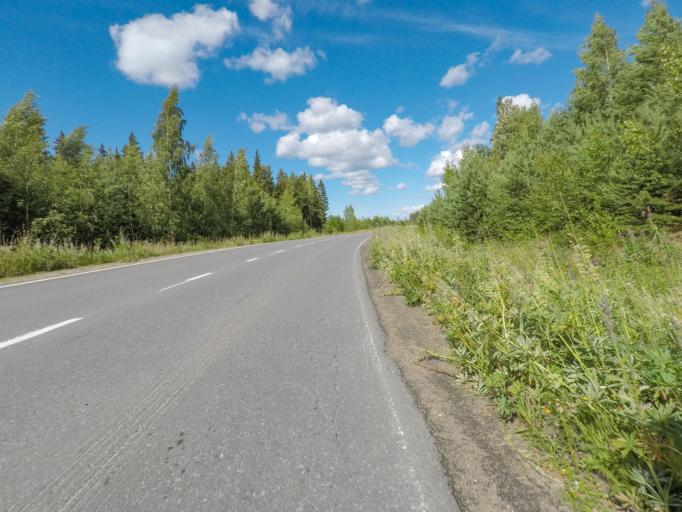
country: FI
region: South Karelia
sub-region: Lappeenranta
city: Joutseno
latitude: 61.0933
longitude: 28.3526
